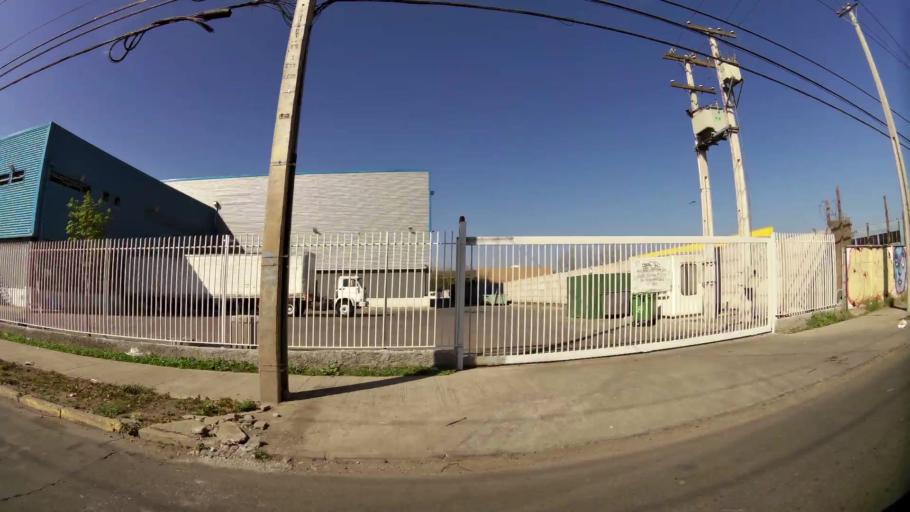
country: CL
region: Santiago Metropolitan
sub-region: Provincia de Chacabuco
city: Chicureo Abajo
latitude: -33.3622
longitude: -70.6791
